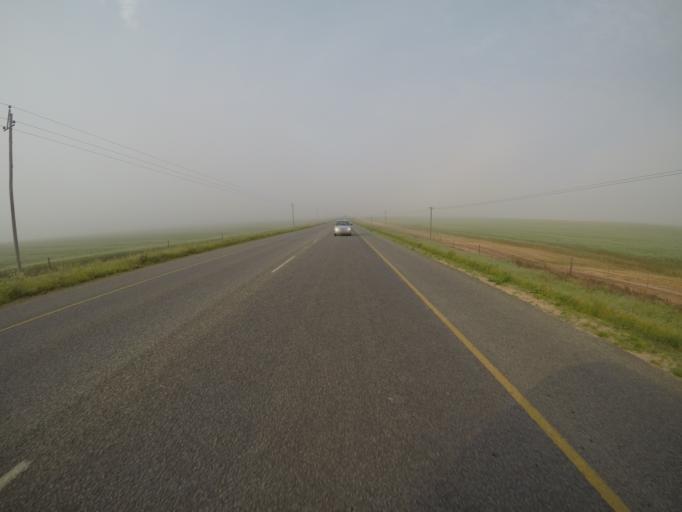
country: ZA
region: Western Cape
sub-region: West Coast District Municipality
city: Malmesbury
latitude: -33.6441
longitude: 18.7142
